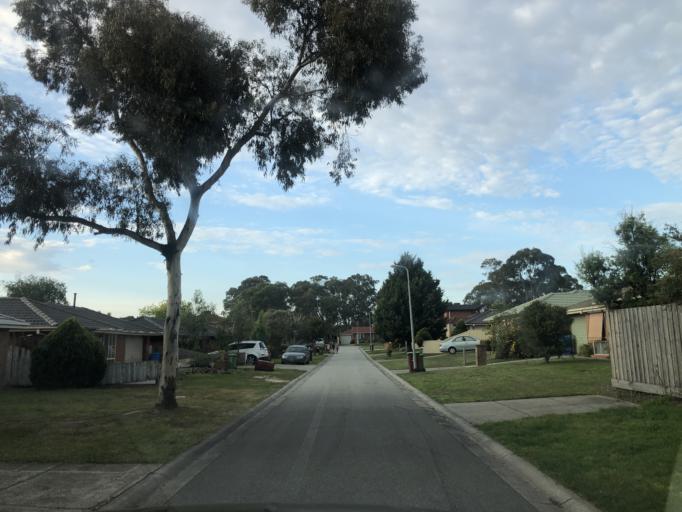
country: AU
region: Victoria
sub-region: Casey
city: Hampton Park
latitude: -38.0297
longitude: 145.2517
